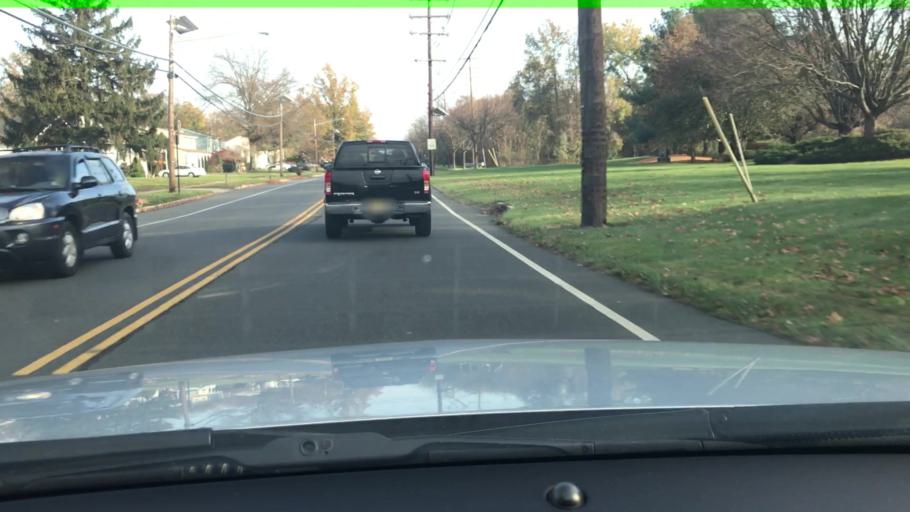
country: US
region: New Jersey
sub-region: Mercer County
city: Mercerville
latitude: 40.2233
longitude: -74.6836
